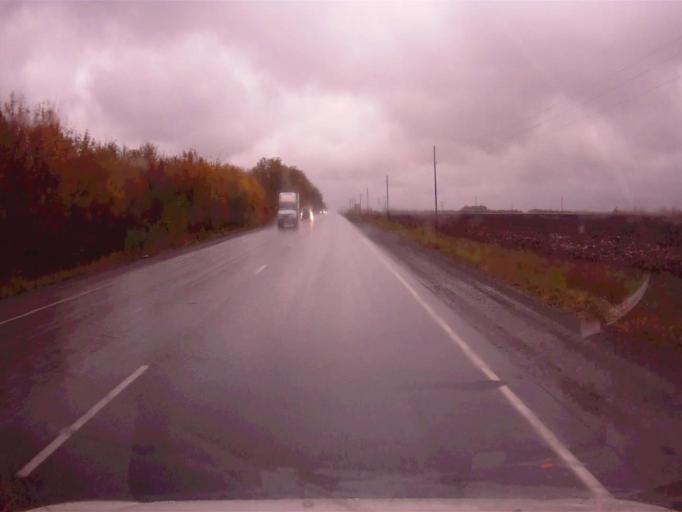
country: RU
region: Chelyabinsk
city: Argayash
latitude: 55.4287
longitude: 60.9952
